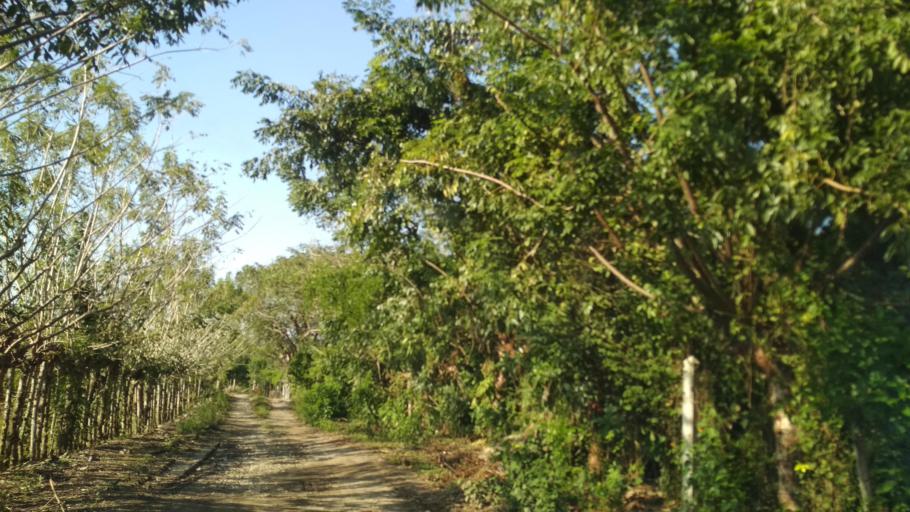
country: MX
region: Veracruz
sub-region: Martinez de la Torre
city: El Progreso
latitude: 20.0862
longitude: -97.0201
